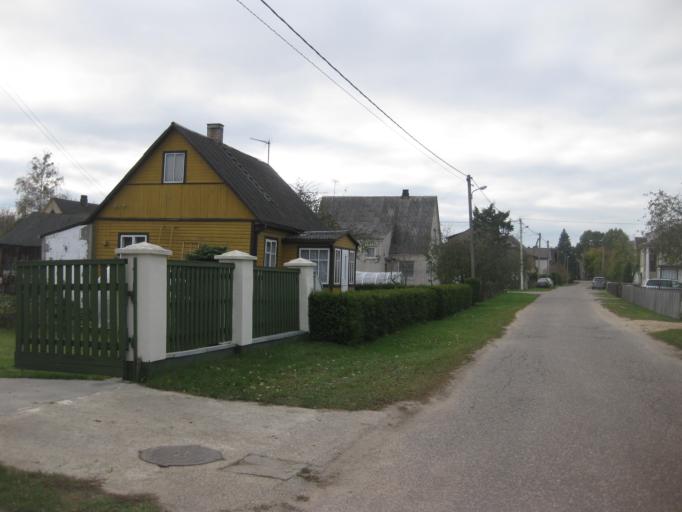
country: LT
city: Ezerelis
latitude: 54.8841
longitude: 23.6030
